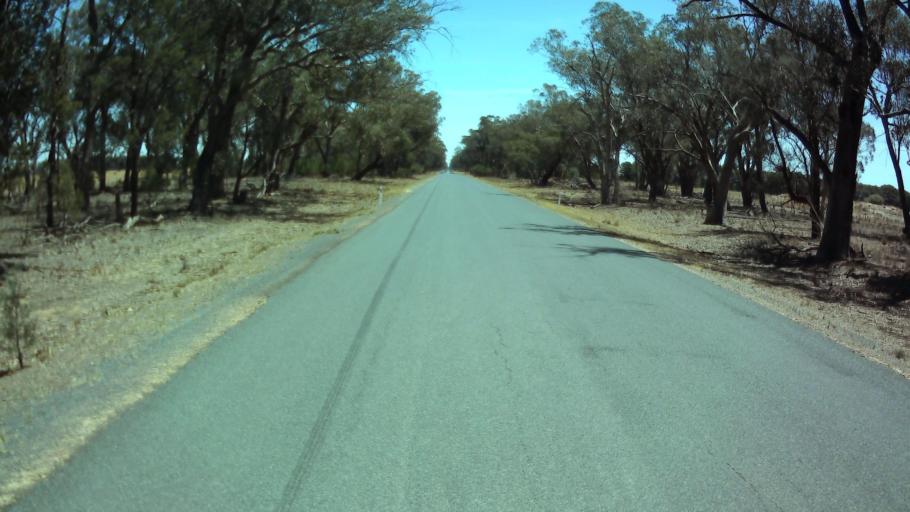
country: AU
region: New South Wales
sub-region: Weddin
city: Grenfell
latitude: -34.0255
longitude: 147.8723
